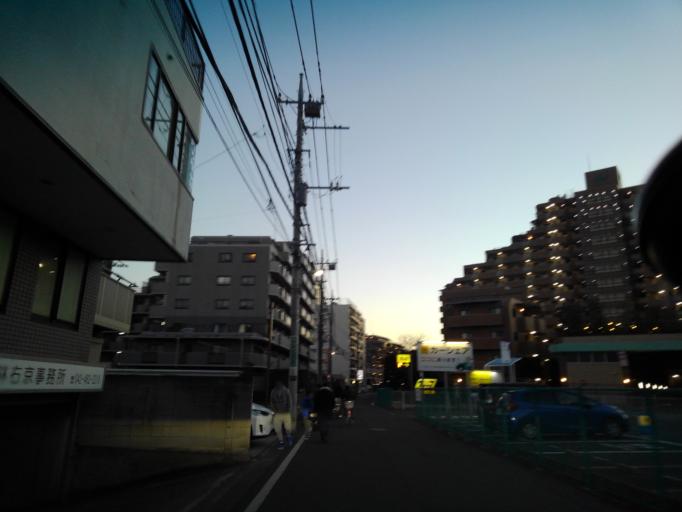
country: JP
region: Tokyo
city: Chofugaoka
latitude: 35.6480
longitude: 139.5680
